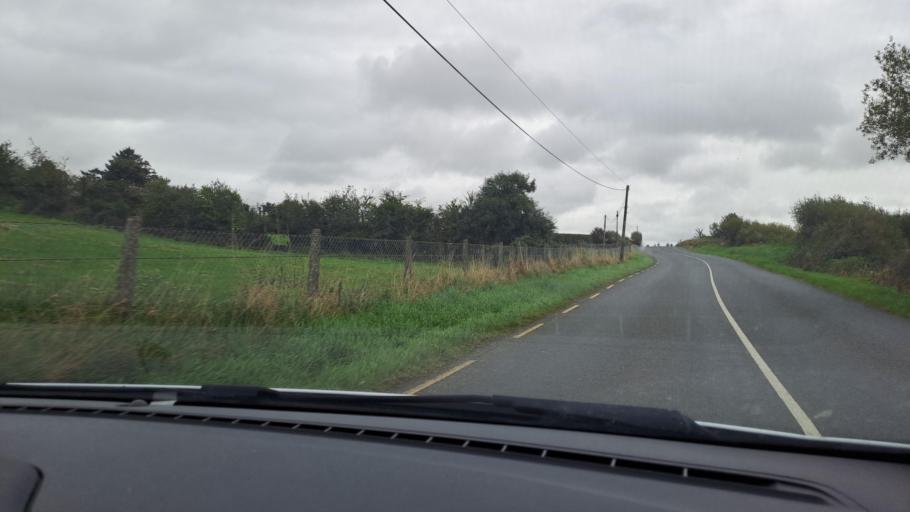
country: IE
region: Ulster
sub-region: County Monaghan
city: Carrickmacross
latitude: 54.0363
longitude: -6.7858
